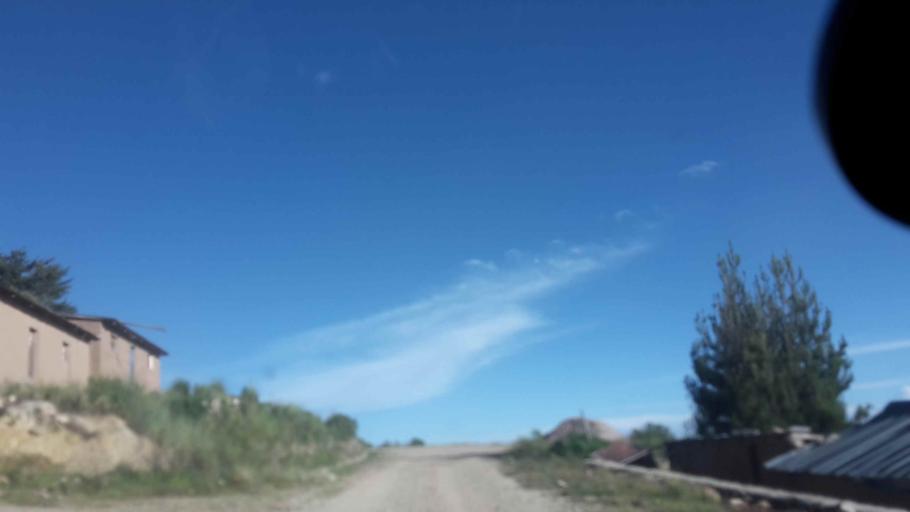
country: BO
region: Cochabamba
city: Arani
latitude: -17.7106
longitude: -65.6912
